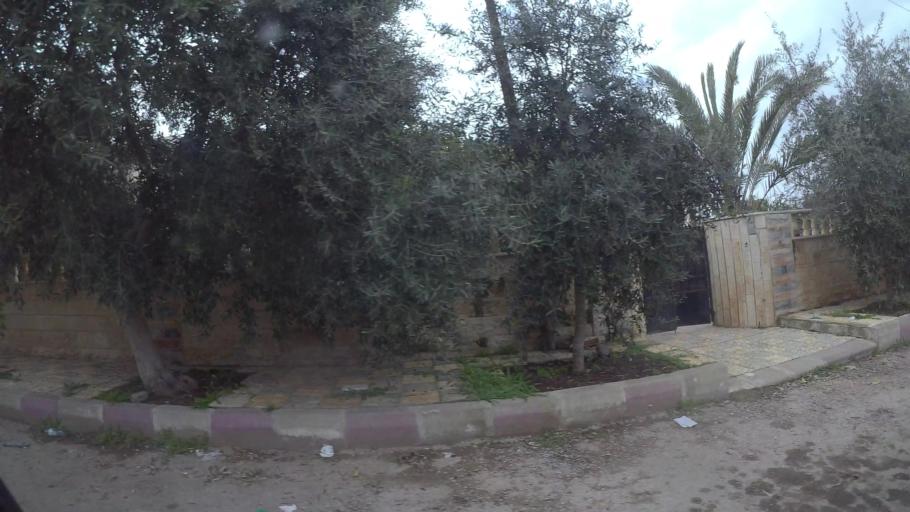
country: JO
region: Amman
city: Al Jubayhah
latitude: 32.0561
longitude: 35.8272
